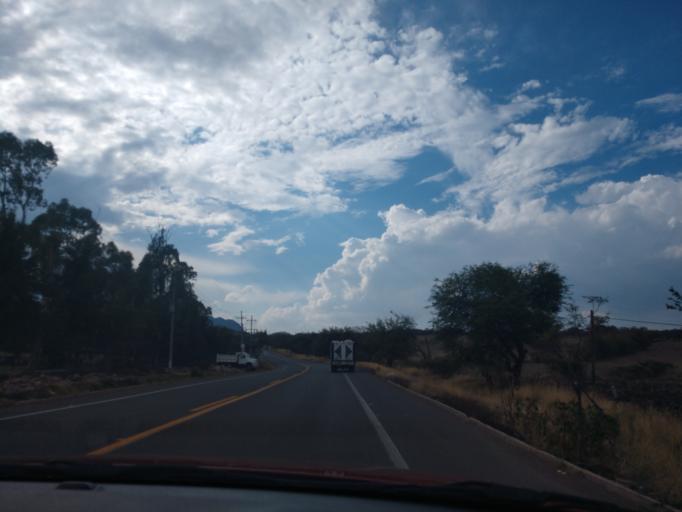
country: MX
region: Jalisco
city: Chapala
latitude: 20.1541
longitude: -103.1881
